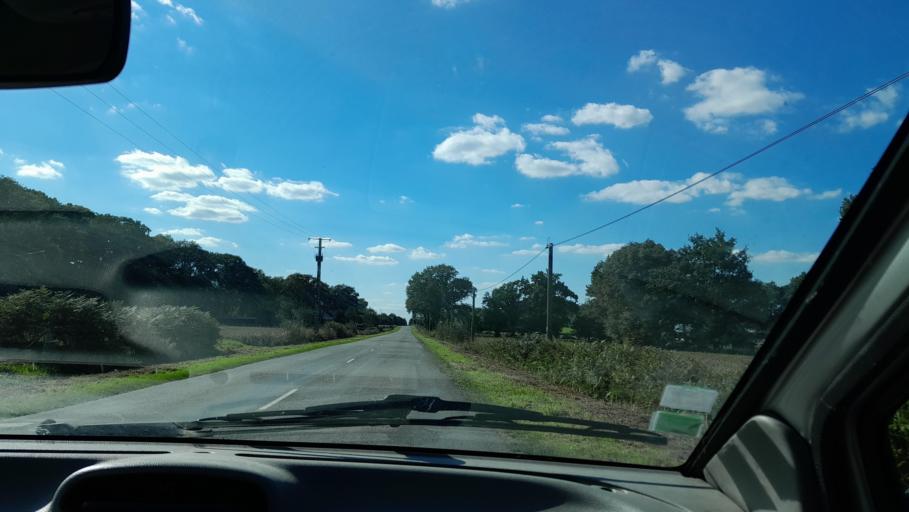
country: FR
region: Brittany
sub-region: Departement d'Ille-et-Vilaine
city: Le Pertre
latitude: 47.9687
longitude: -1.0894
